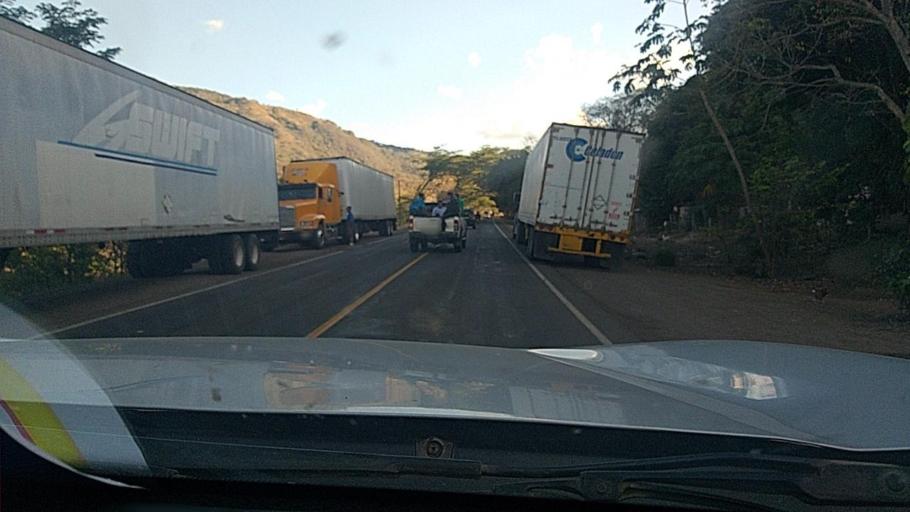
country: NI
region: Esteli
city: Condega
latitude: 13.2919
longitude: -86.3472
